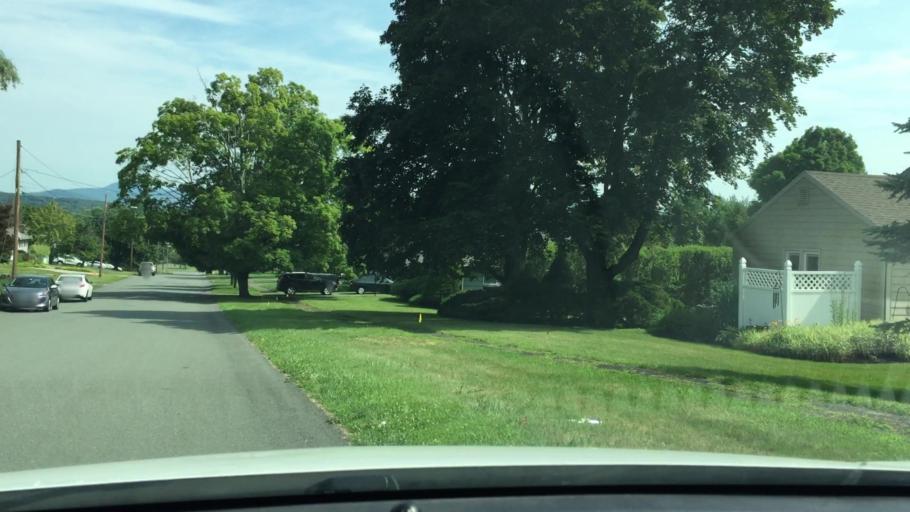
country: US
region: Massachusetts
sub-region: Berkshire County
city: Pittsfield
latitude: 42.4340
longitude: -73.2231
